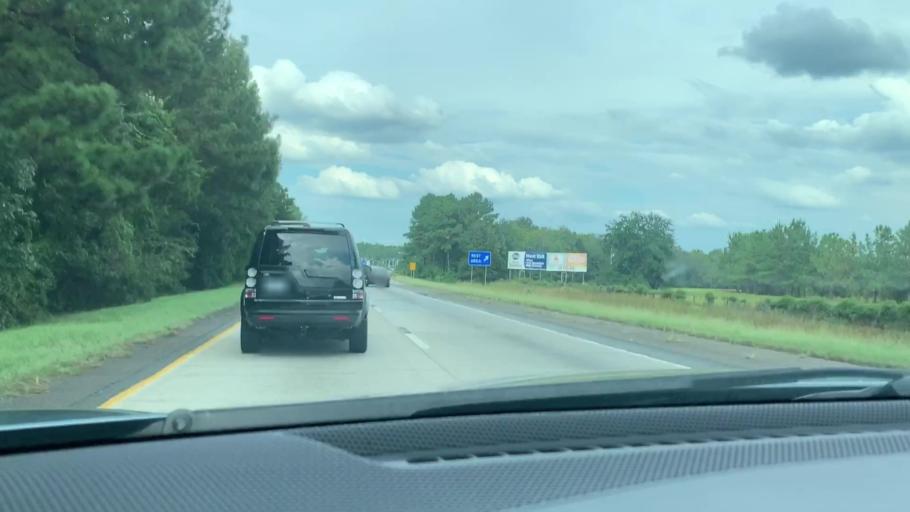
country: US
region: South Carolina
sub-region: Hampton County
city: Yemassee
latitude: 32.7959
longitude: -80.7736
